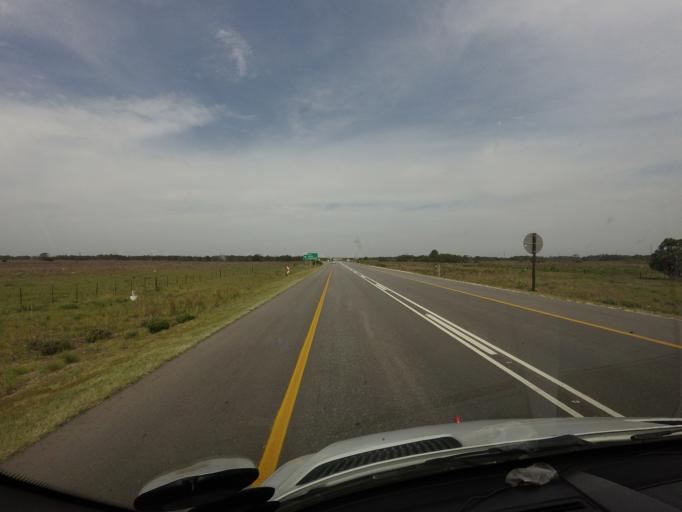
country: ZA
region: Eastern Cape
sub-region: Cacadu District Municipality
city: Kruisfontein
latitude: -34.0047
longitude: 24.7726
